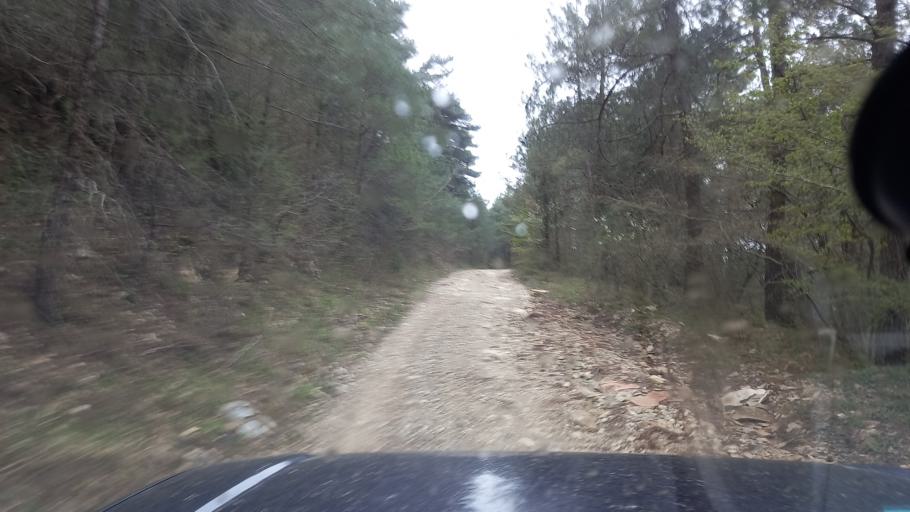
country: RU
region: Krasnodarskiy
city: Arkhipo-Osipovka
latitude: 44.3711
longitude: 38.4516
